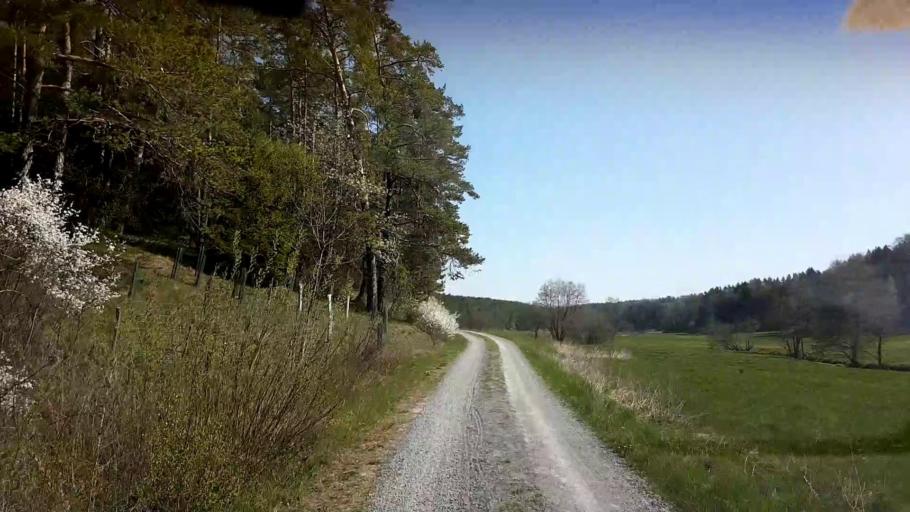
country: DE
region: Bavaria
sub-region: Upper Franconia
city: Konigsfeld
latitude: 49.9383
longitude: 11.1927
